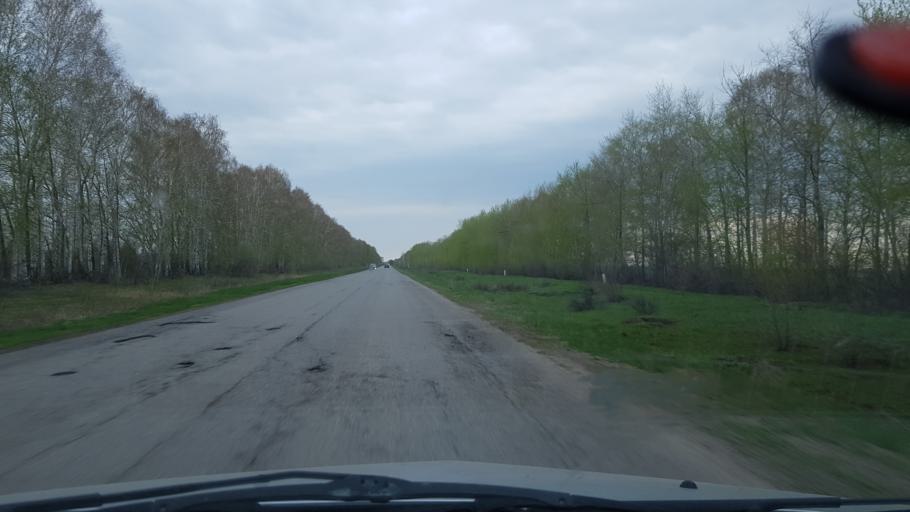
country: RU
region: Samara
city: Podstepki
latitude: 53.6628
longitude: 49.1960
